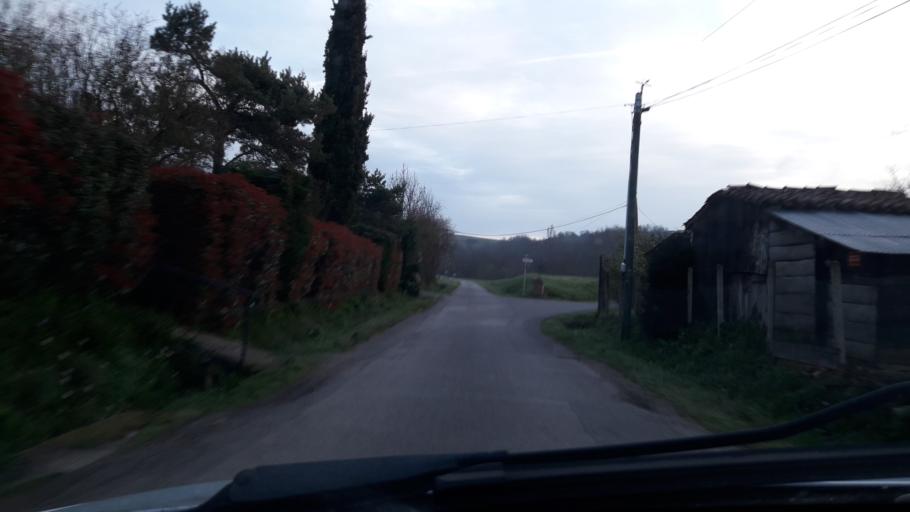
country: FR
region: Midi-Pyrenees
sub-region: Departement de la Haute-Garonne
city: Montesquieu-Volvestre
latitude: 43.1685
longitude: 1.2763
